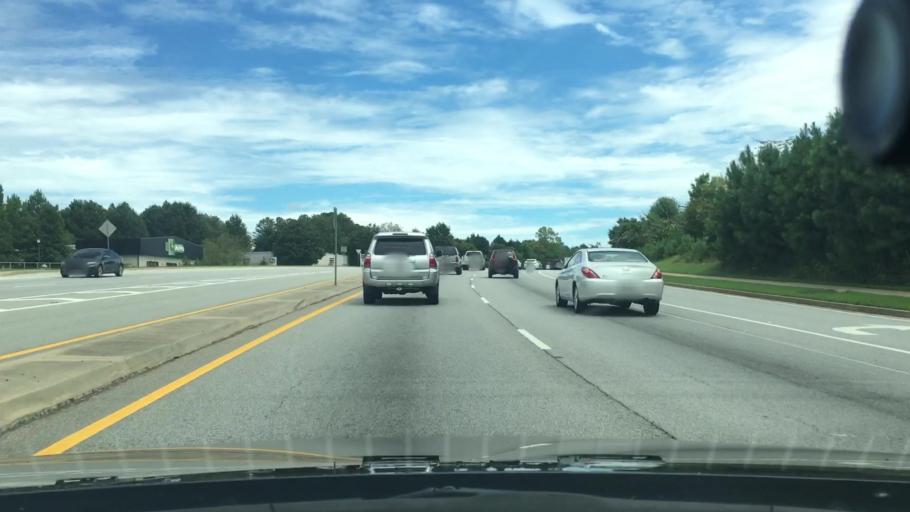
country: US
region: Georgia
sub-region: Coweta County
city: Newnan
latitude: 33.4003
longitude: -84.7689
